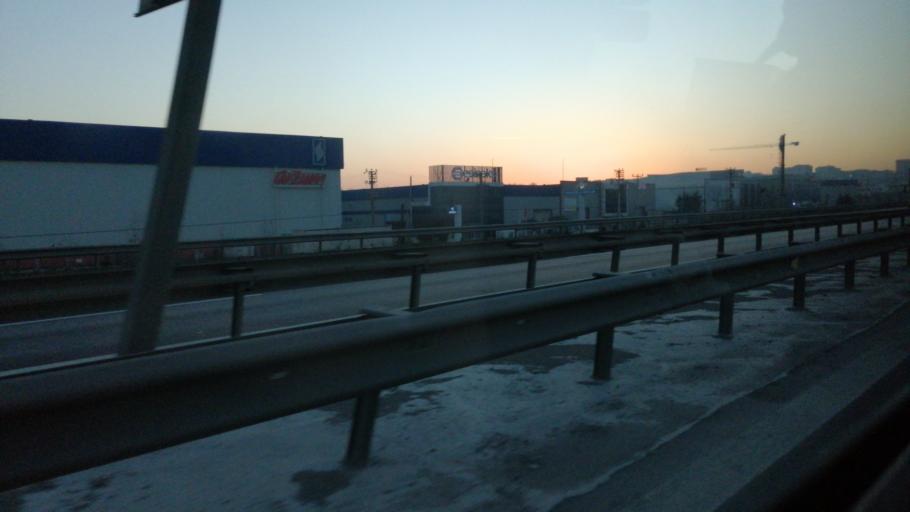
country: TR
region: Kocaeli
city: Gebze
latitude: 40.8087
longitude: 29.4675
